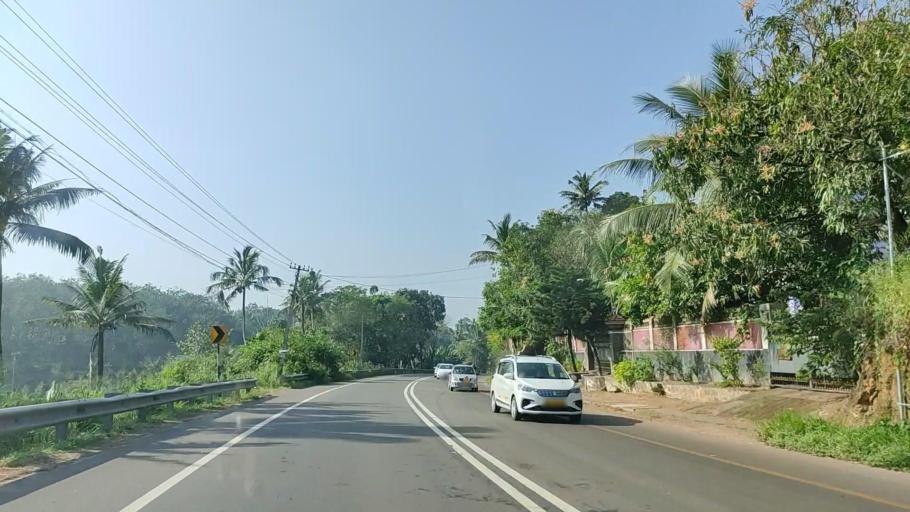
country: IN
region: Kerala
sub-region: Kollam
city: Punalur
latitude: 8.8829
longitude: 76.8692
